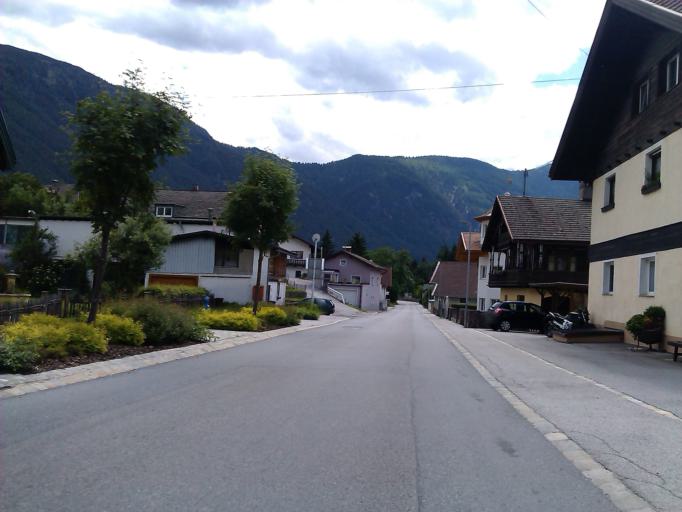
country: AT
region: Tyrol
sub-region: Politischer Bezirk Imst
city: Nassereith
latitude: 47.3114
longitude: 10.8399
